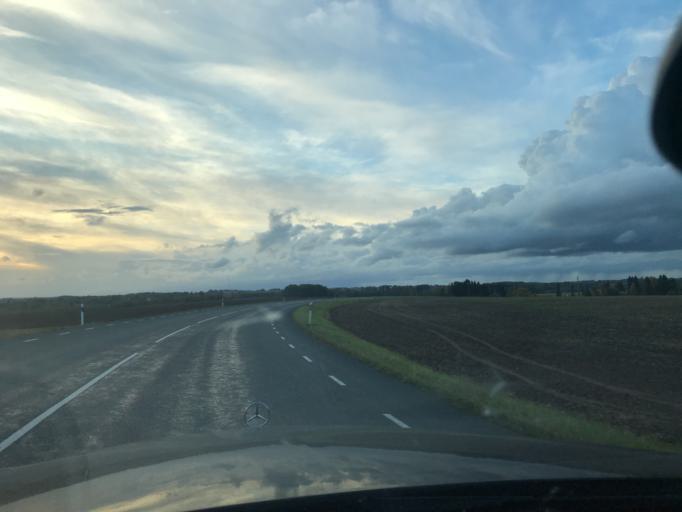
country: EE
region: Vorumaa
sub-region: Antsla vald
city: Vana-Antsla
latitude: 57.9161
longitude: 26.3568
